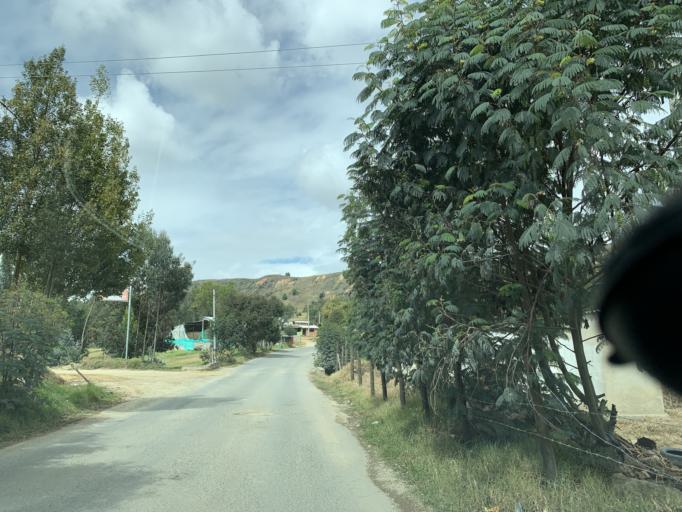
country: CO
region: Boyaca
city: Siachoque
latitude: 5.5681
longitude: -73.2644
